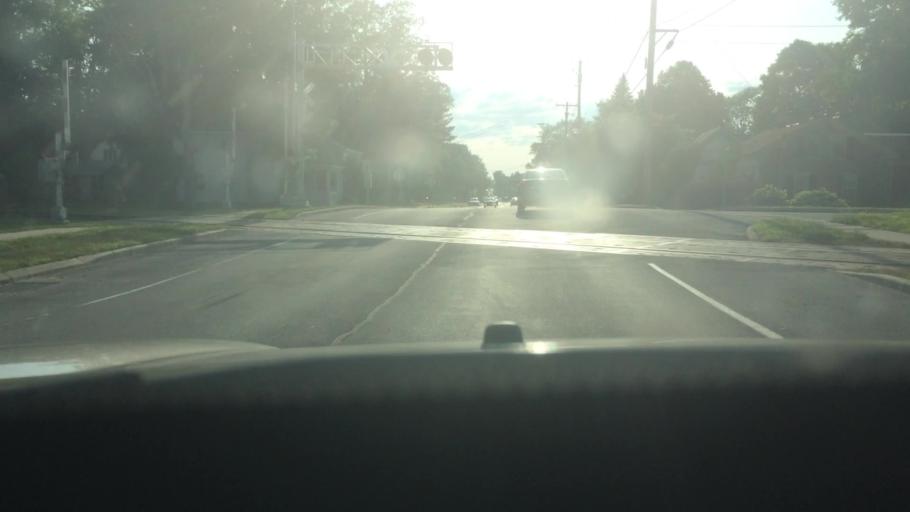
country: US
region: New York
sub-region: St. Lawrence County
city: Canton
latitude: 44.5959
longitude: -75.1648
